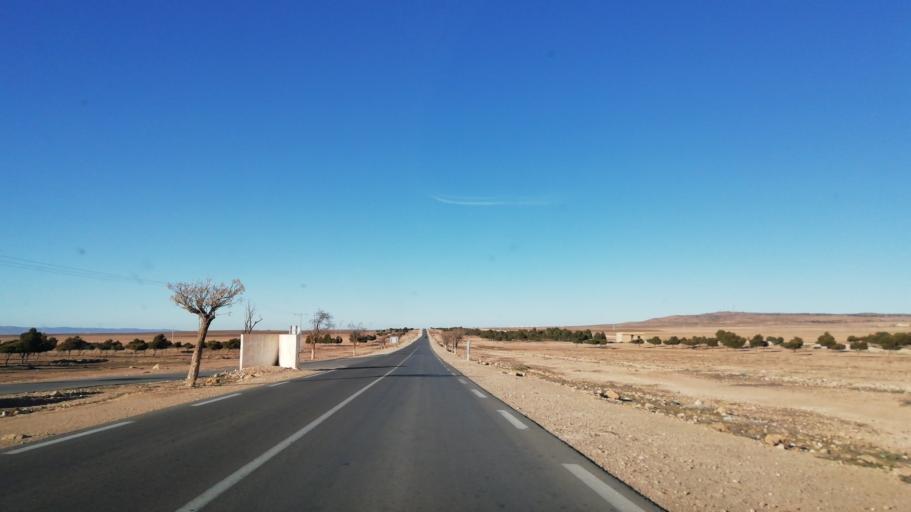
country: DZ
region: Tlemcen
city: Sebdou
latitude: 34.2334
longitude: -1.2564
